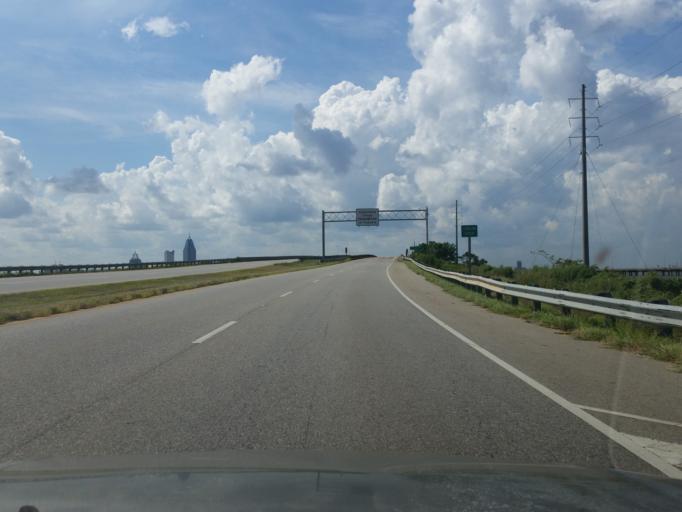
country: US
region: Alabama
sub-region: Mobile County
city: Mobile
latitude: 30.6820
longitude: -88.0059
